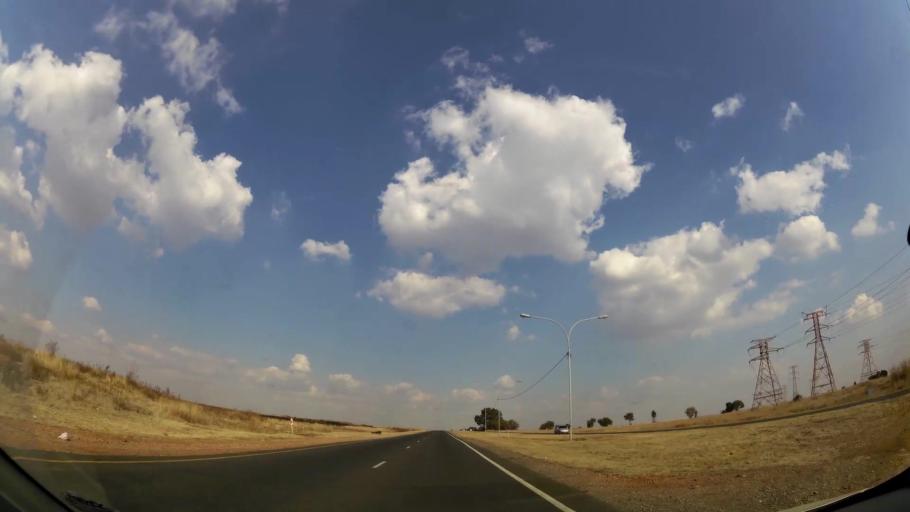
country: ZA
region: Gauteng
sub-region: Ekurhuleni Metropolitan Municipality
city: Brakpan
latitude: -26.2765
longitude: 28.3286
